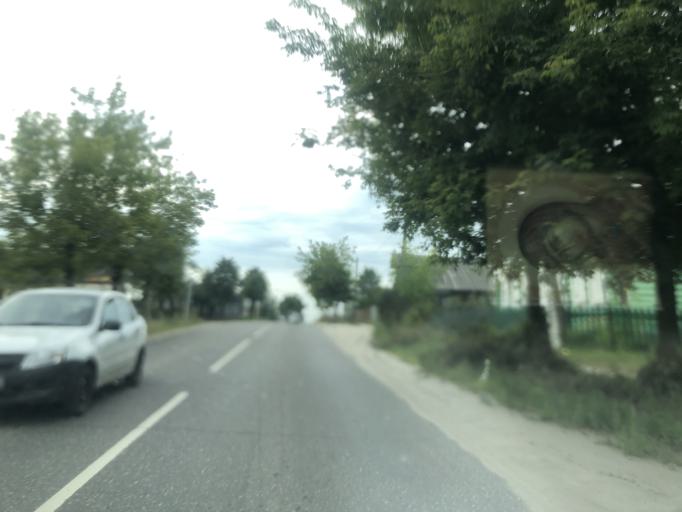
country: RU
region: Ivanovo
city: Pestyaki
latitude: 56.7083
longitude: 42.6684
